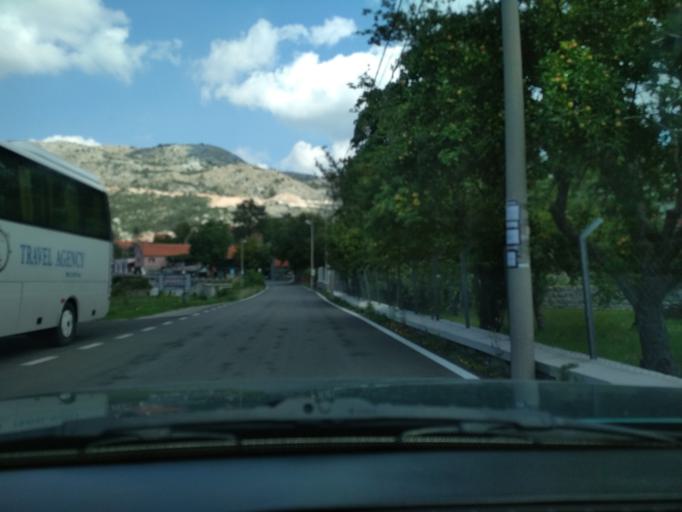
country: ME
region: Kotor
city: Kotor
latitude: 42.4312
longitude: 18.8280
